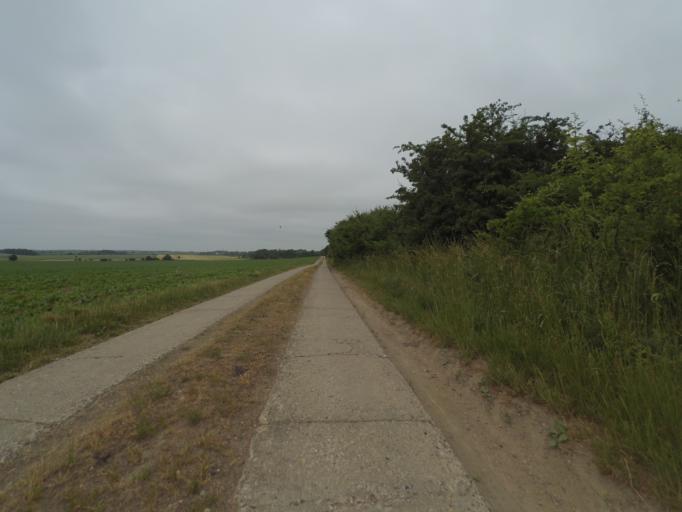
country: DE
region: Mecklenburg-Vorpommern
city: Gaegelow
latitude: 53.6794
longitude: 11.9095
